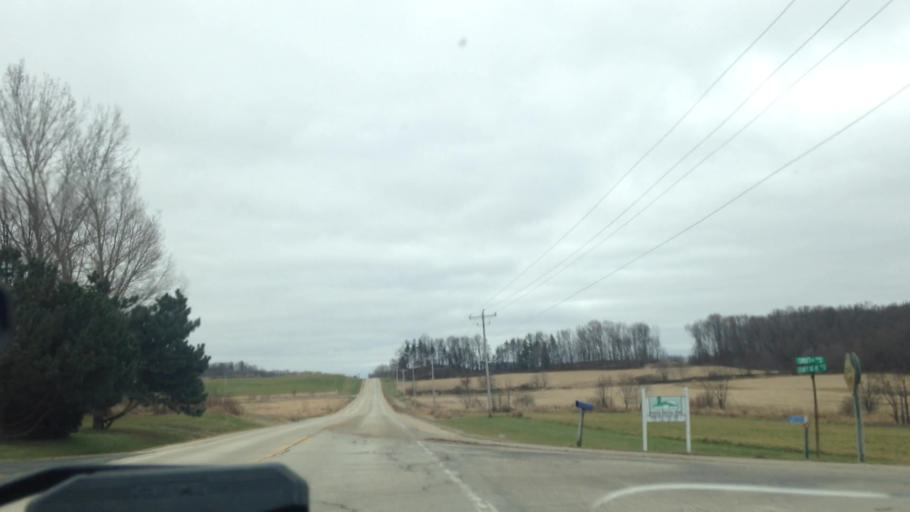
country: US
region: Wisconsin
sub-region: Dodge County
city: Mayville
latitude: 43.4570
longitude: -88.4999
